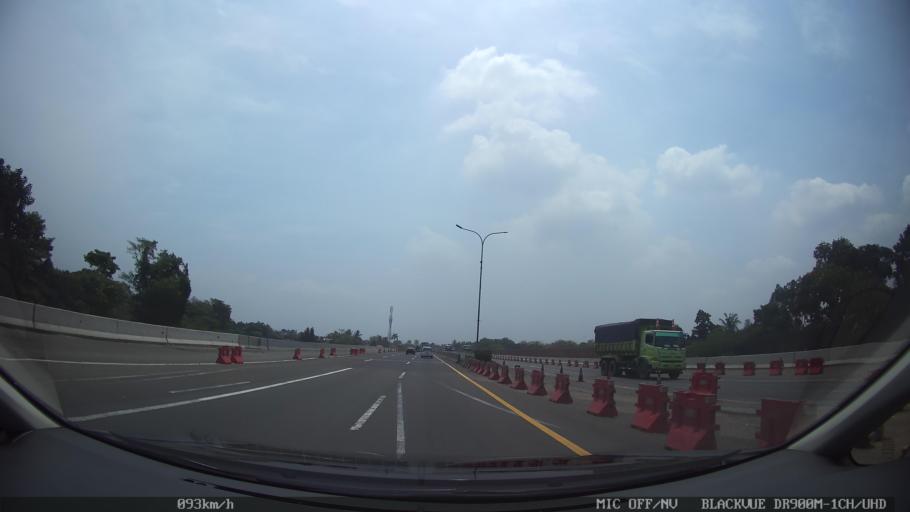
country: ID
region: West Java
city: Kresek
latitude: -6.1520
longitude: 106.3106
